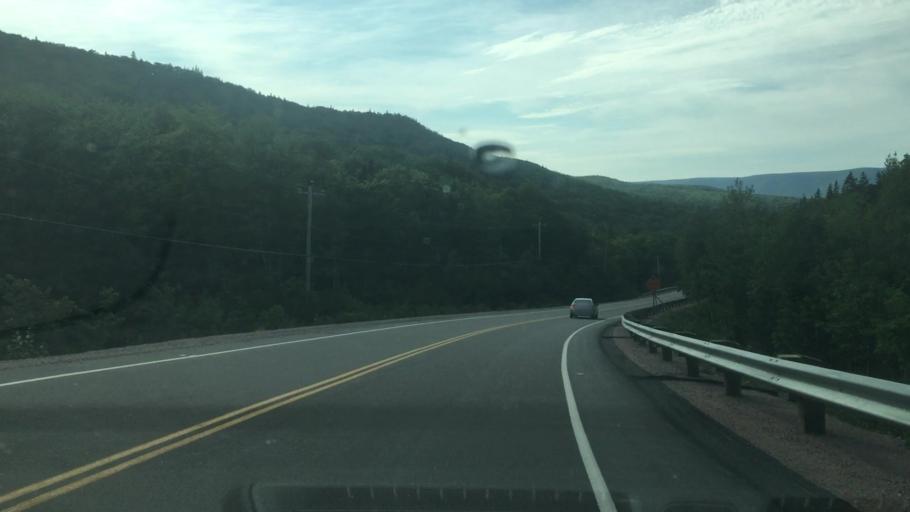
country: CA
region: Nova Scotia
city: Sydney Mines
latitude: 46.8550
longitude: -60.4531
